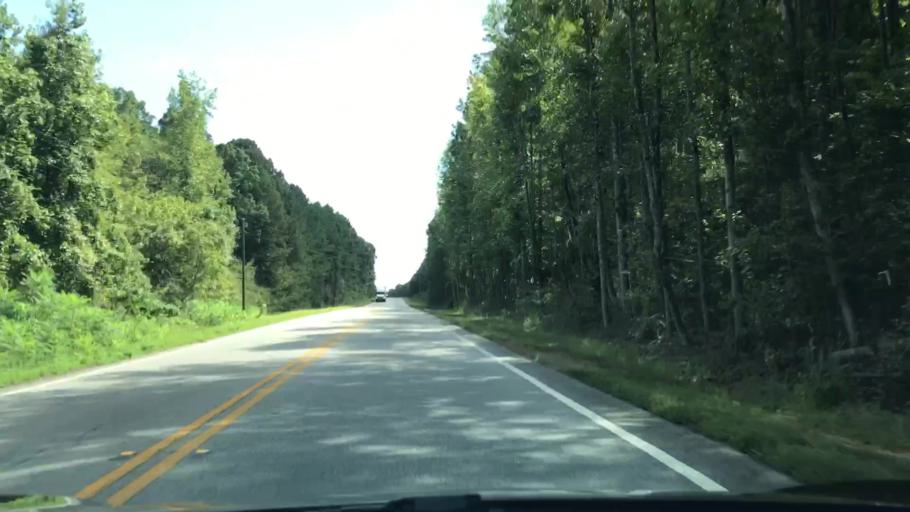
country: US
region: Georgia
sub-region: Greene County
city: Greensboro
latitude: 33.6880
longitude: -83.2746
